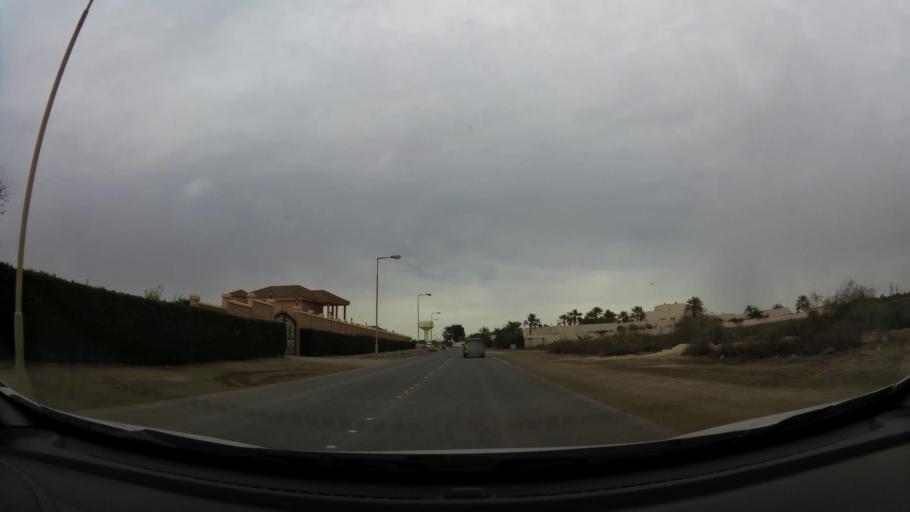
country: BH
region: Central Governorate
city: Madinat Hamad
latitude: 26.1359
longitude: 50.4640
